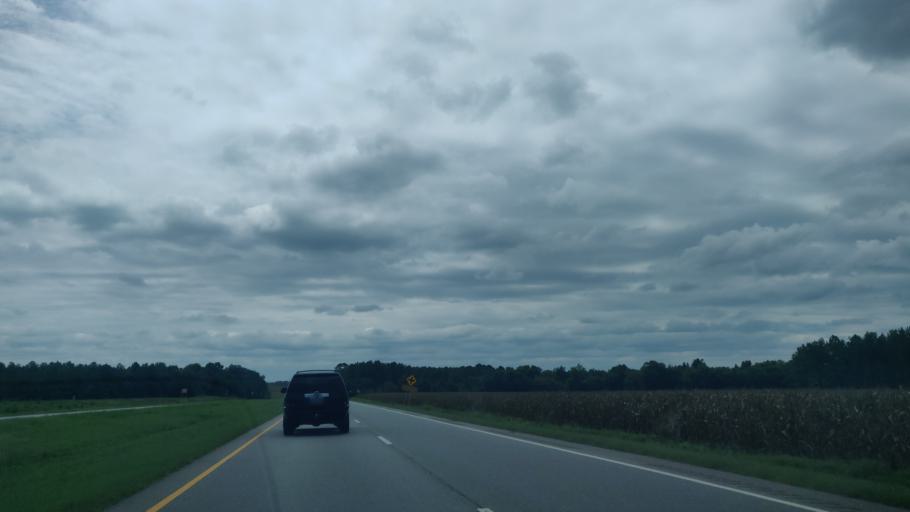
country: US
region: Georgia
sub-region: Terrell County
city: Dawson
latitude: 31.8566
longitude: -84.4798
